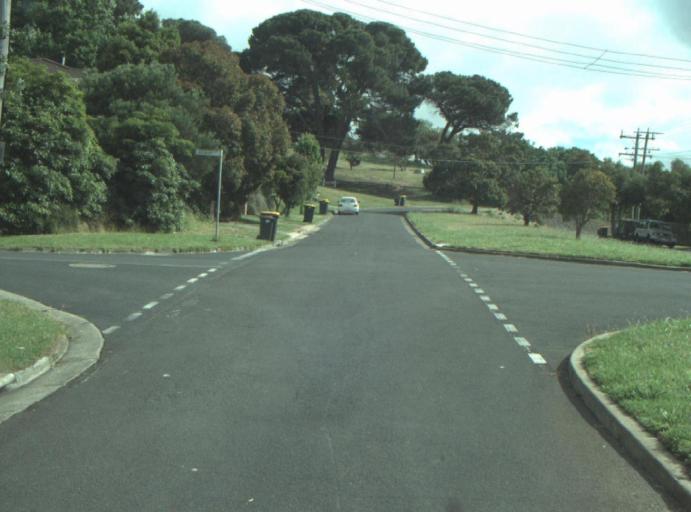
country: AU
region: Victoria
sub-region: Greater Geelong
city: Wandana Heights
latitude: -38.1642
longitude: 144.3152
